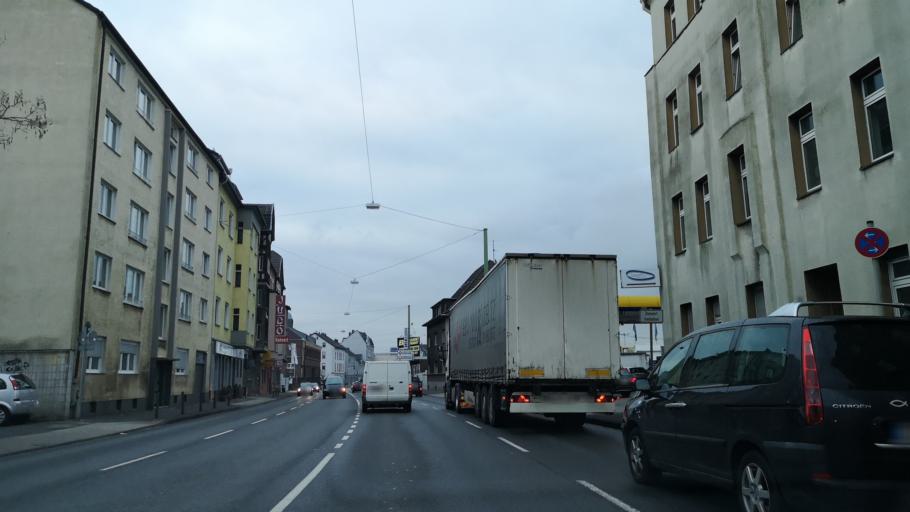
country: DE
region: North Rhine-Westphalia
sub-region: Regierungsbezirk Arnsberg
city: Hagen
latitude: 51.3511
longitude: 7.4418
